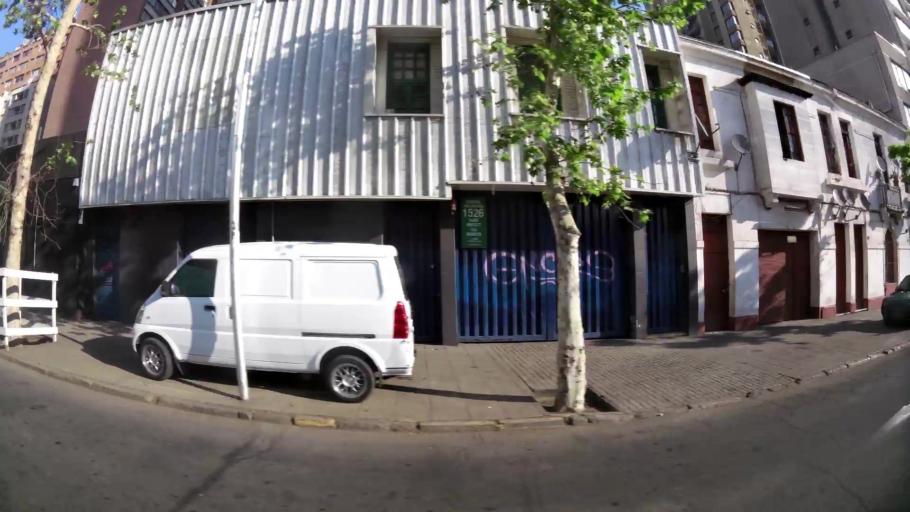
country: CL
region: Santiago Metropolitan
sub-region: Provincia de Santiago
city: Santiago
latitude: -33.4334
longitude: -70.6594
